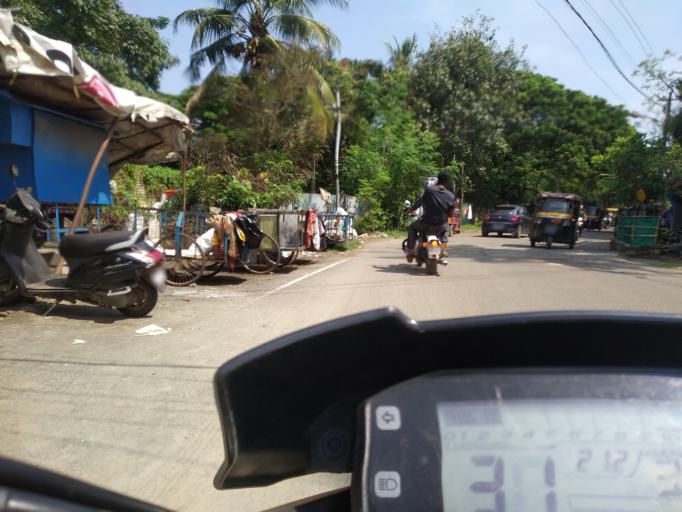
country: IN
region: Kerala
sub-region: Ernakulam
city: Cochin
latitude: 9.9743
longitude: 76.2929
